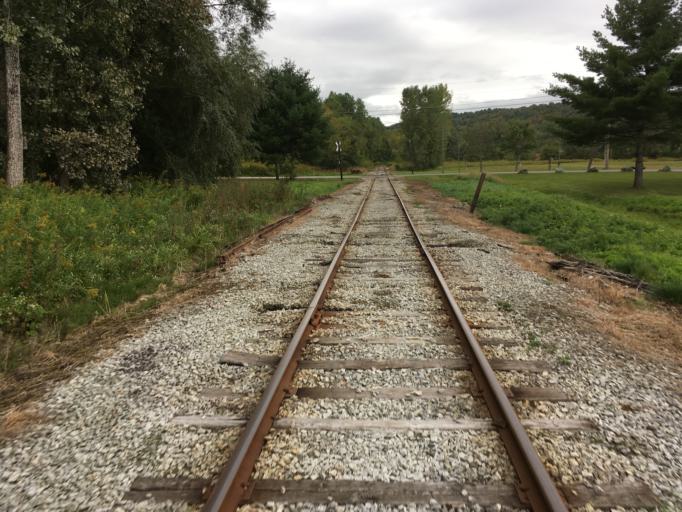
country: US
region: Vermont
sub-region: Washington County
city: Montpelier
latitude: 44.2326
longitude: -72.5499
